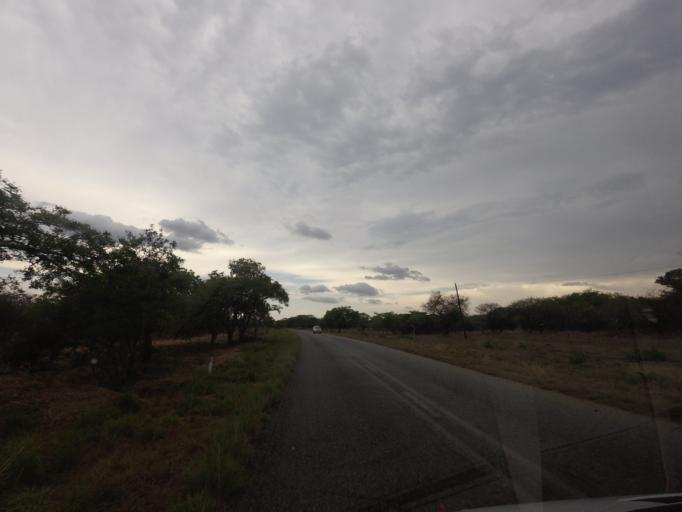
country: ZA
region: Limpopo
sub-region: Mopani District Municipality
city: Hoedspruit
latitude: -24.5138
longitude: 30.9464
